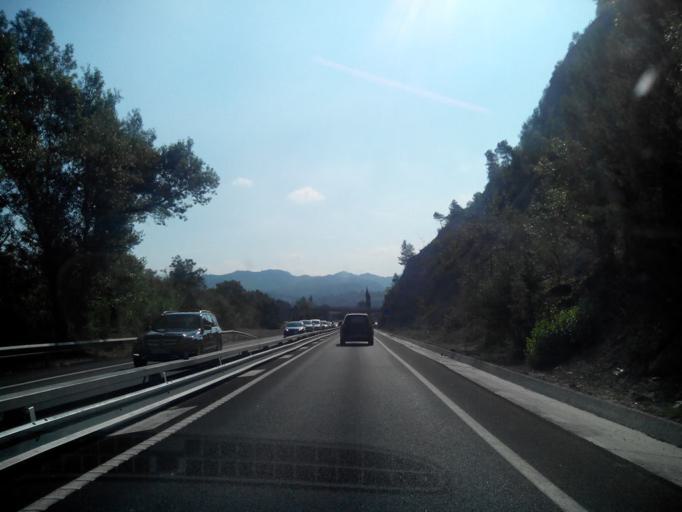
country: ES
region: Catalonia
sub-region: Provincia de Barcelona
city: Manresa
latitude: 41.6788
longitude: 1.8416
